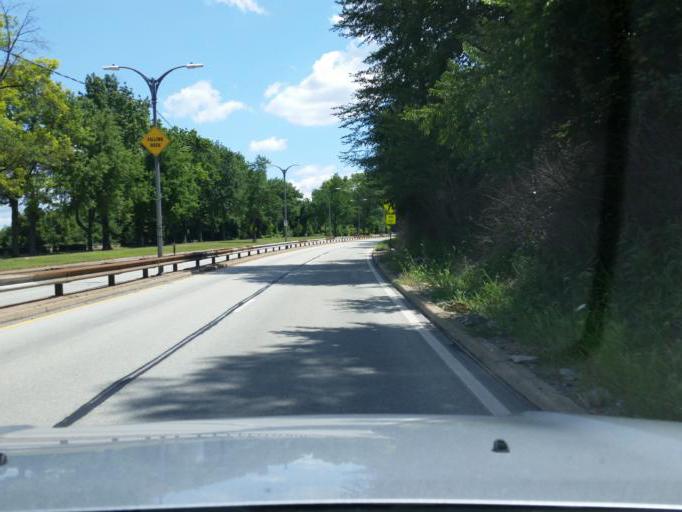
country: US
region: Pennsylvania
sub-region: Allegheny County
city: Pittsburgh
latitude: 40.4498
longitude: -79.9813
